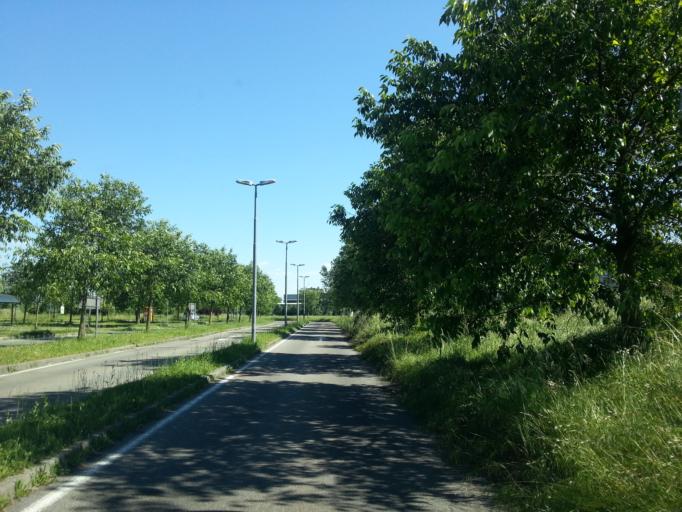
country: IT
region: Lombardy
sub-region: Provincia di Monza e Brianza
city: Varedo
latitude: 45.5888
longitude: 9.1748
